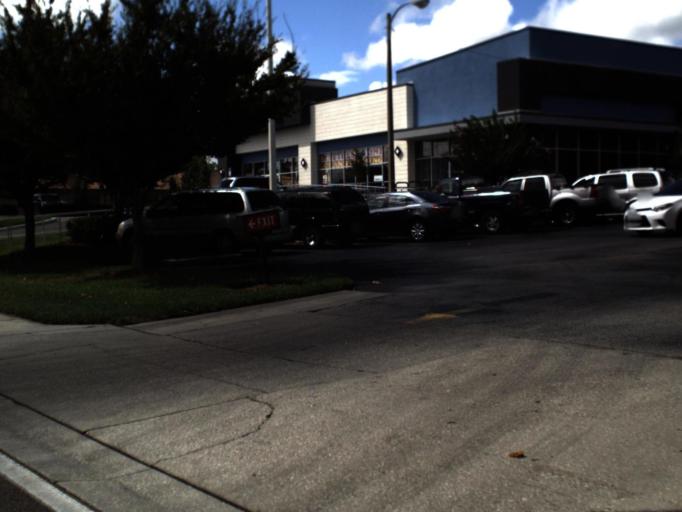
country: US
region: Florida
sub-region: Polk County
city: Medulla
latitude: 27.9926
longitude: -81.9570
